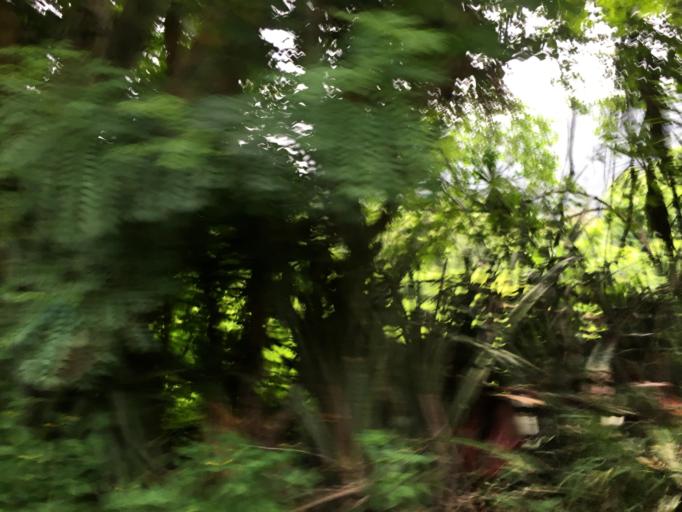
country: GT
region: Guatemala
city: Villa Canales
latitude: 14.4197
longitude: -90.5438
